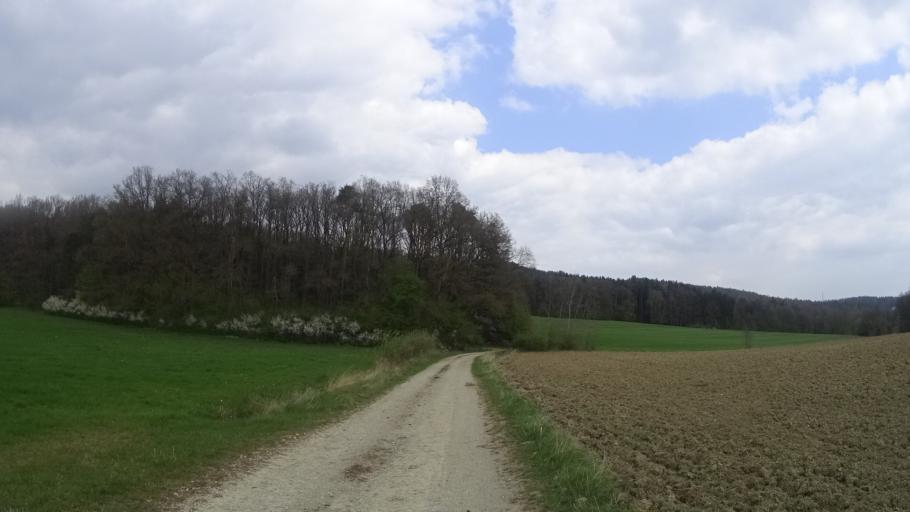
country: DE
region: Bavaria
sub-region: Upper Franconia
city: Kleinsendelbach
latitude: 49.6137
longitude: 11.1810
